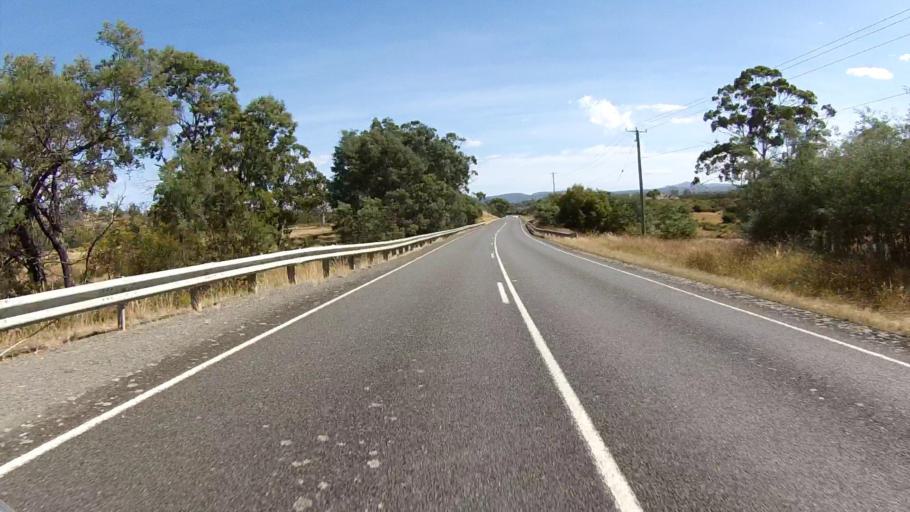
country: AU
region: Tasmania
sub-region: Sorell
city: Sorell
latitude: -42.5924
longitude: 147.7954
